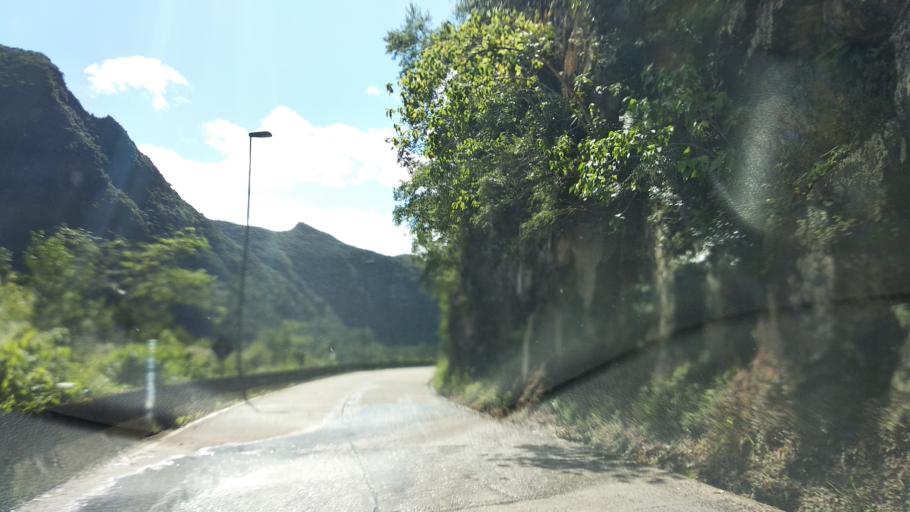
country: BR
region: Santa Catarina
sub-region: Lauro Muller
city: Lauro Muller
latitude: -28.3923
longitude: -49.5333
